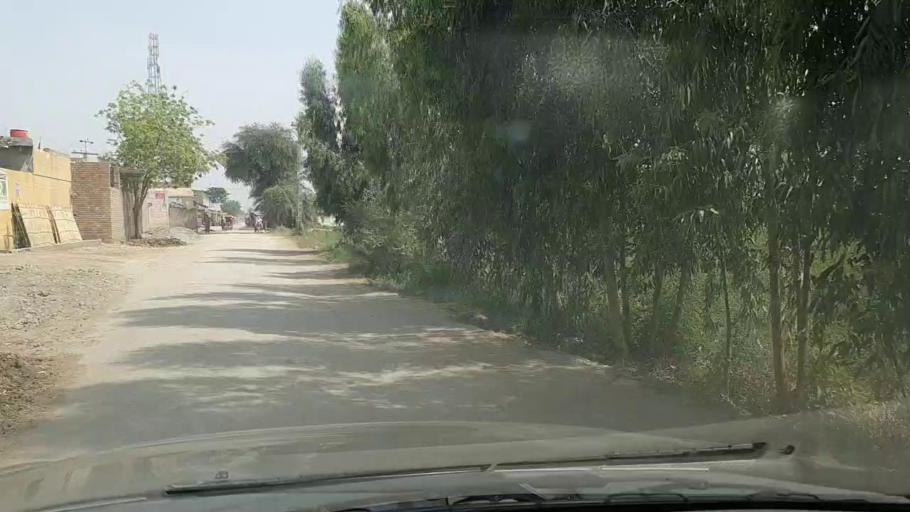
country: PK
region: Sindh
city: Shikarpur
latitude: 27.9298
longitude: 68.6610
